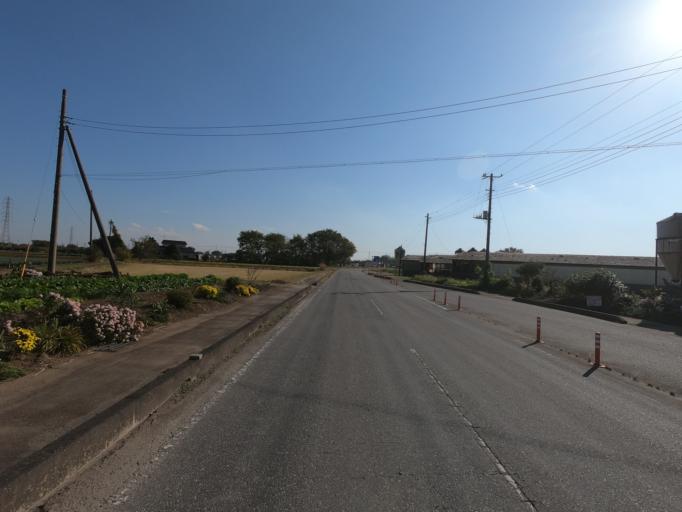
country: JP
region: Ibaraki
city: Tsukuba
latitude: 36.1339
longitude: 140.1494
